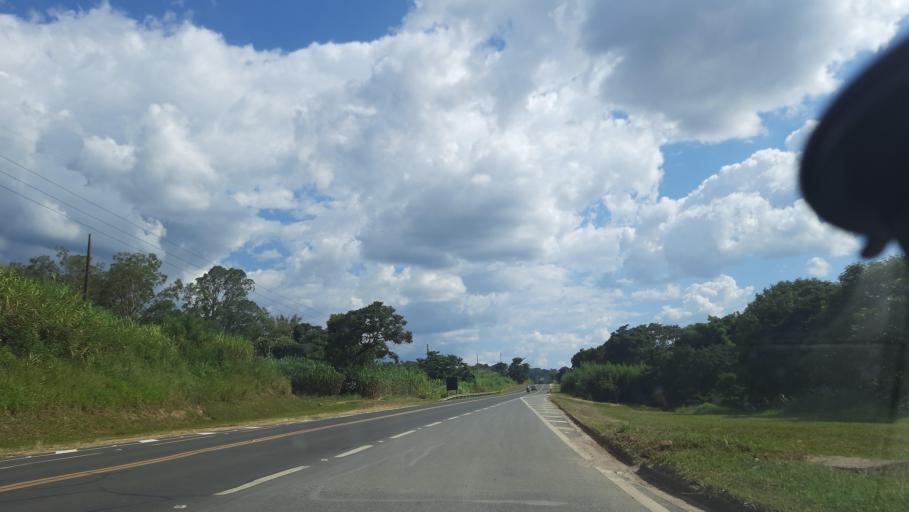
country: BR
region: Sao Paulo
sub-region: Sao Jose Do Rio Pardo
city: Sao Jose do Rio Pardo
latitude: -21.6376
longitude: -46.9048
